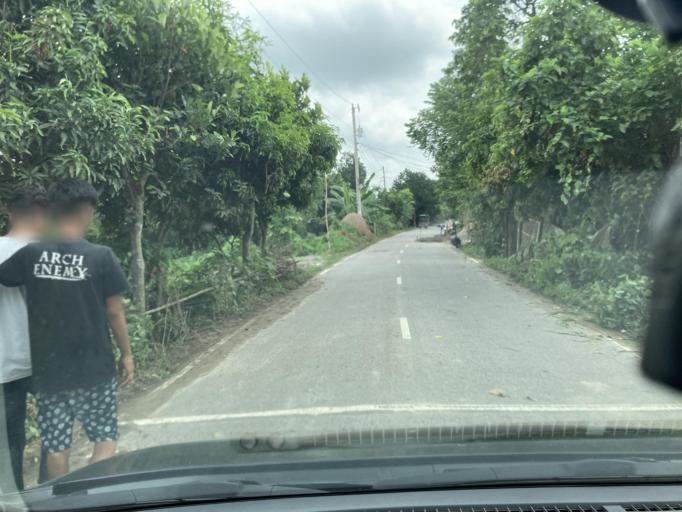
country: BD
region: Dhaka
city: Azimpur
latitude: 23.7869
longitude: 90.2142
